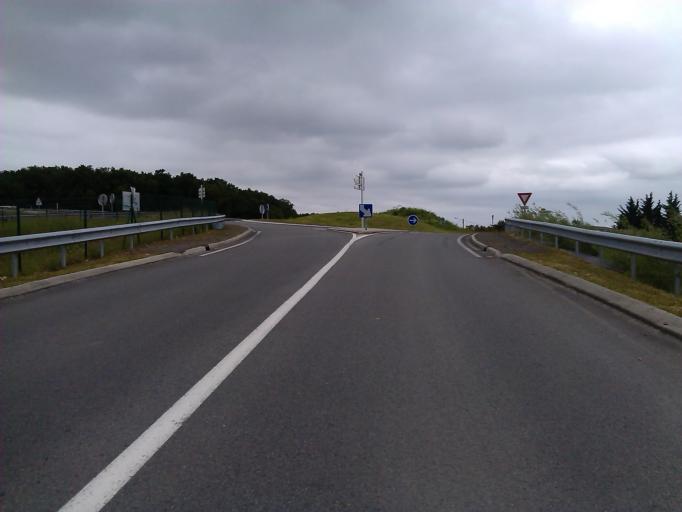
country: FR
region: Poitou-Charentes
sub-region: Departement de la Charente
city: Barbezieux-Saint-Hilaire
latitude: 45.5223
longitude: -0.0981
